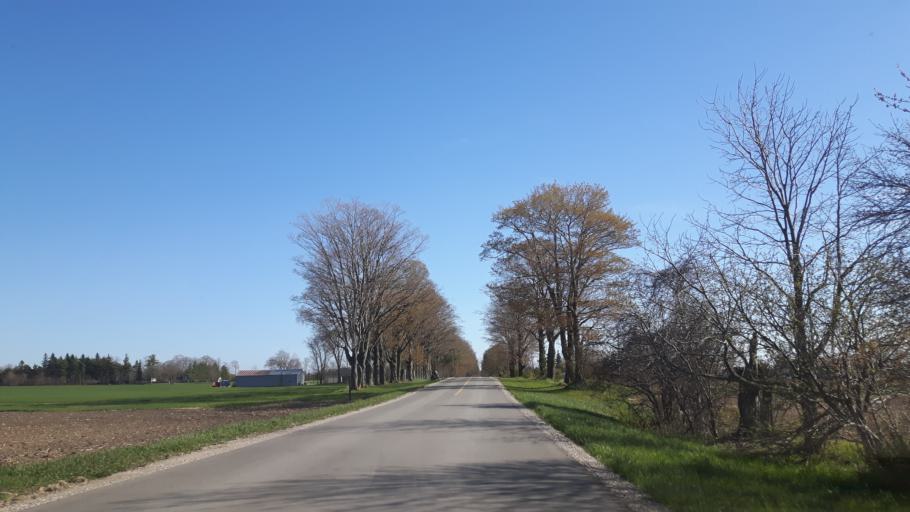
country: CA
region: Ontario
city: Goderich
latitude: 43.6285
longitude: -81.6644
